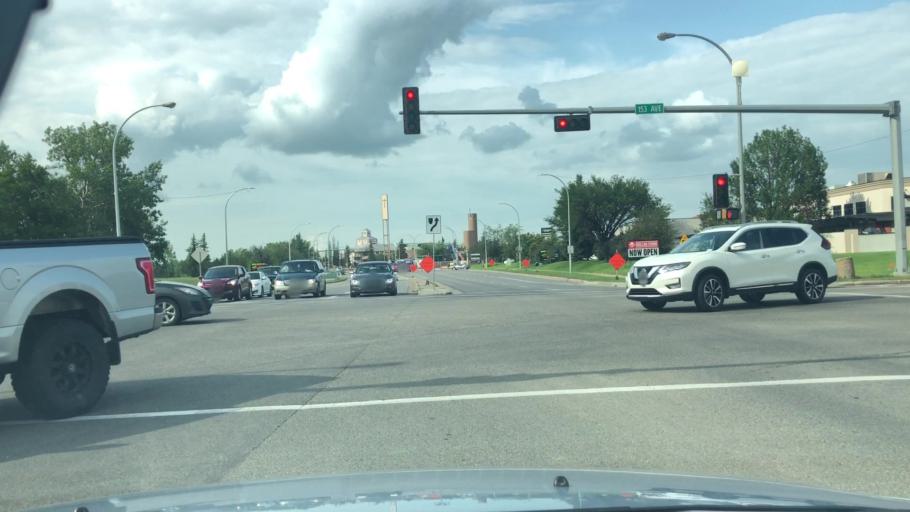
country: CA
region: Alberta
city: Edmonton
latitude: 53.6140
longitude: -113.5167
